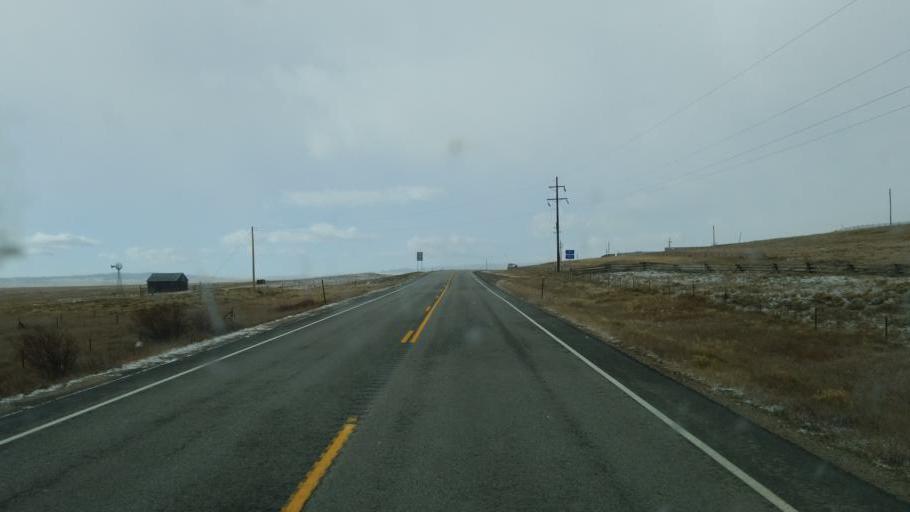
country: US
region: Colorado
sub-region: Summit County
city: Breckenridge
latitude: 39.3889
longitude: -105.7886
